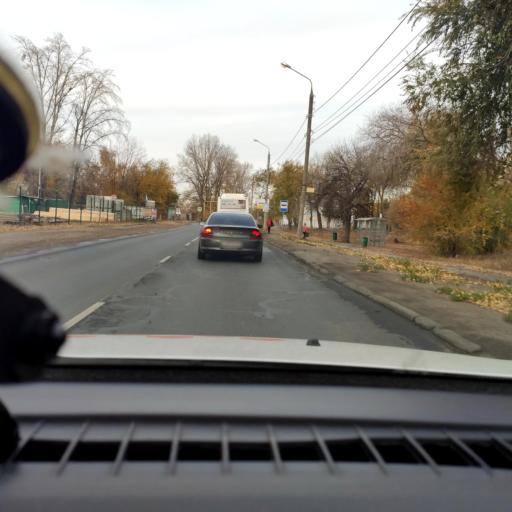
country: RU
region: Samara
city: Rozhdestveno
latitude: 53.1433
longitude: 50.0386
